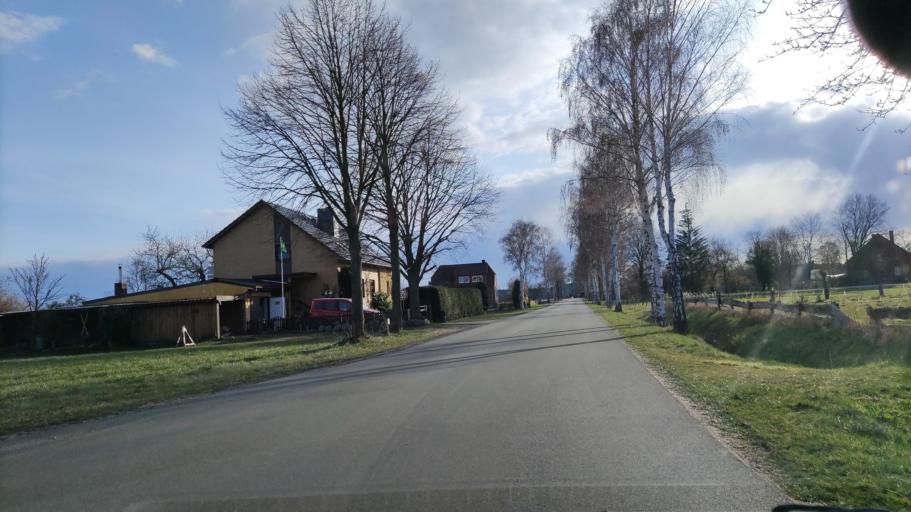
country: DE
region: Lower Saxony
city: Klein Gusborn
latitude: 53.0557
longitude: 11.2297
